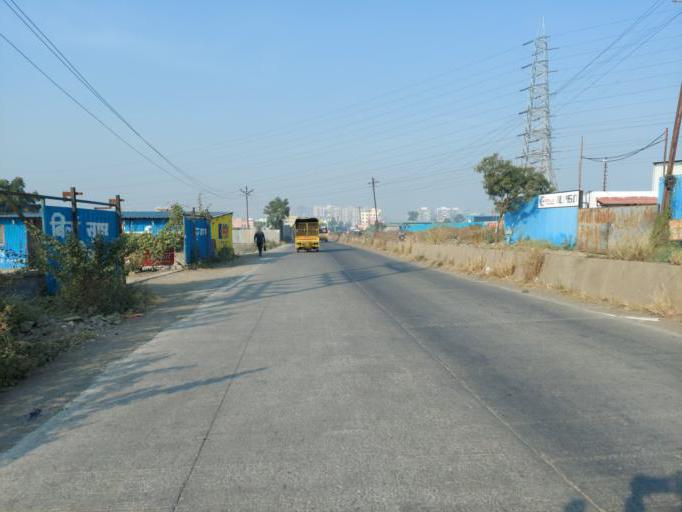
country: IN
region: Maharashtra
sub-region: Pune Division
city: Pune
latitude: 18.4571
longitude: 73.9441
